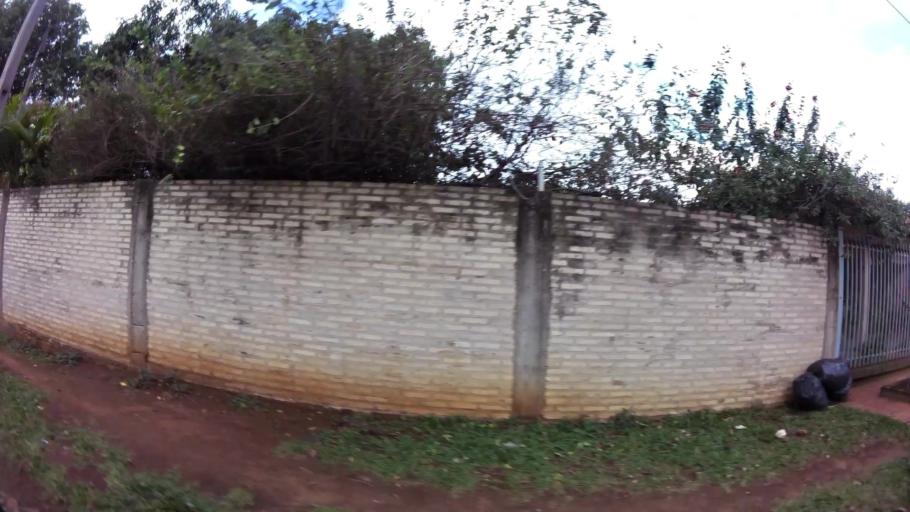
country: PY
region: Central
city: San Lorenzo
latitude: -25.2755
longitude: -57.4892
